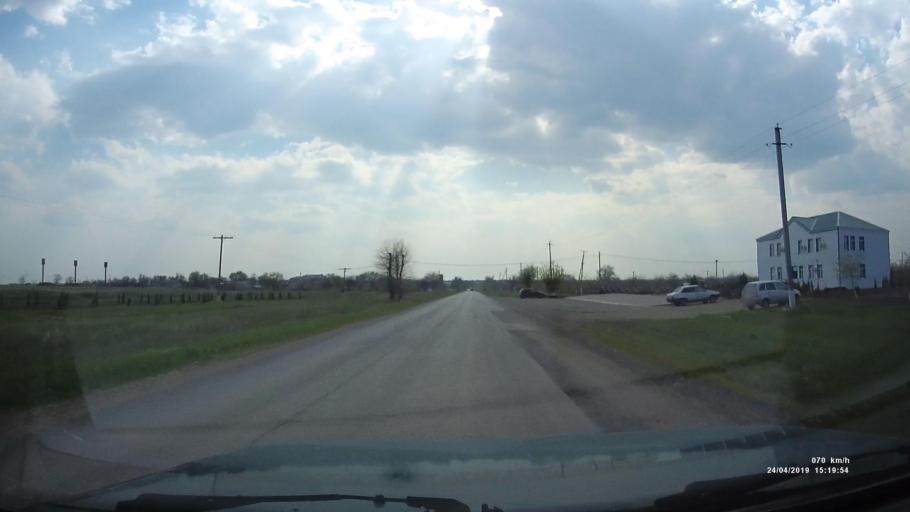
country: RU
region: Rostov
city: Remontnoye
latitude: 46.5377
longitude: 43.1399
